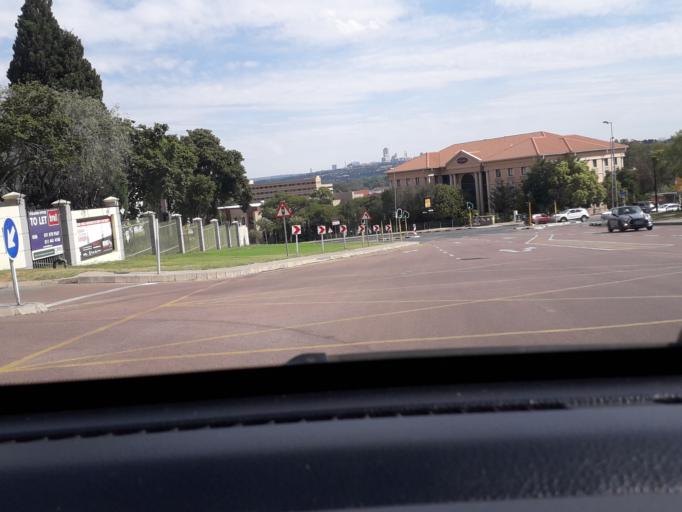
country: ZA
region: Gauteng
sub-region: City of Johannesburg Metropolitan Municipality
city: Midrand
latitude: -26.0336
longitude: 28.0695
